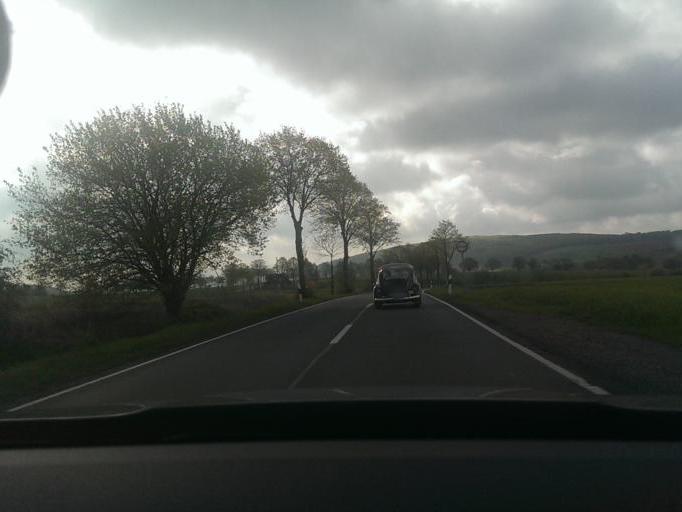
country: DE
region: Lower Saxony
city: Hameln
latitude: 52.1554
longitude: 9.3754
